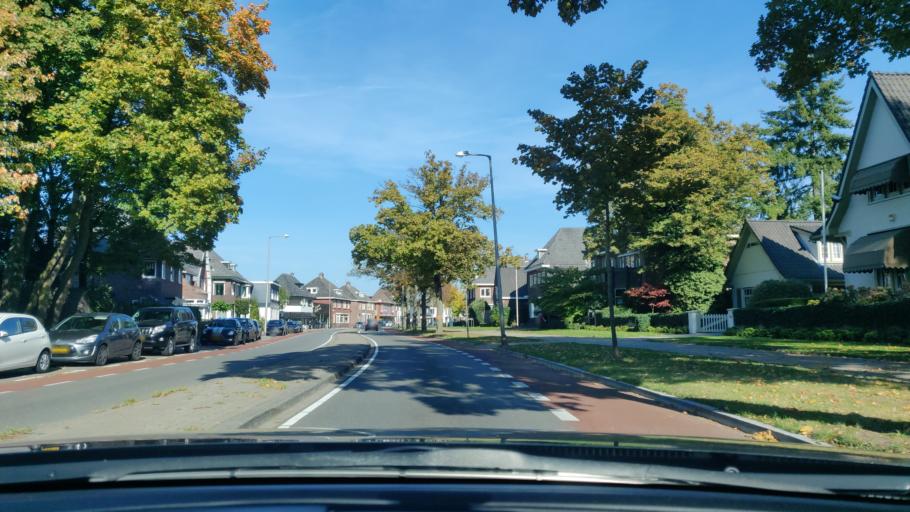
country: NL
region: Overijssel
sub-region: Gemeente Enschede
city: Enschede
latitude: 52.2191
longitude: 6.9122
